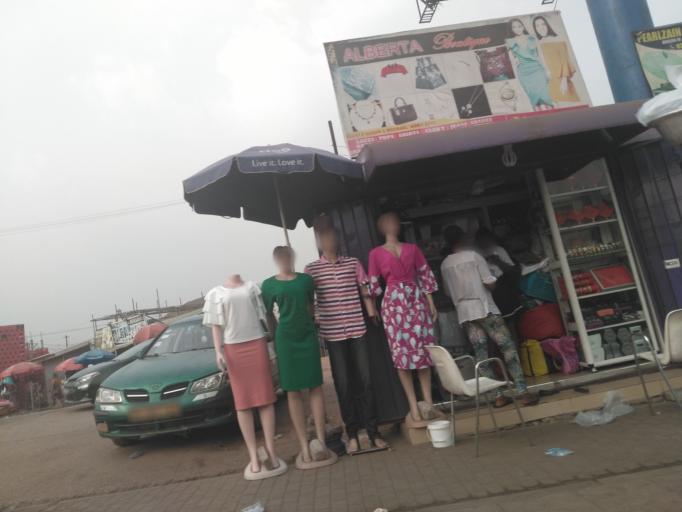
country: GH
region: Ashanti
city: Kumasi
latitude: 6.6869
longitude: -1.5730
